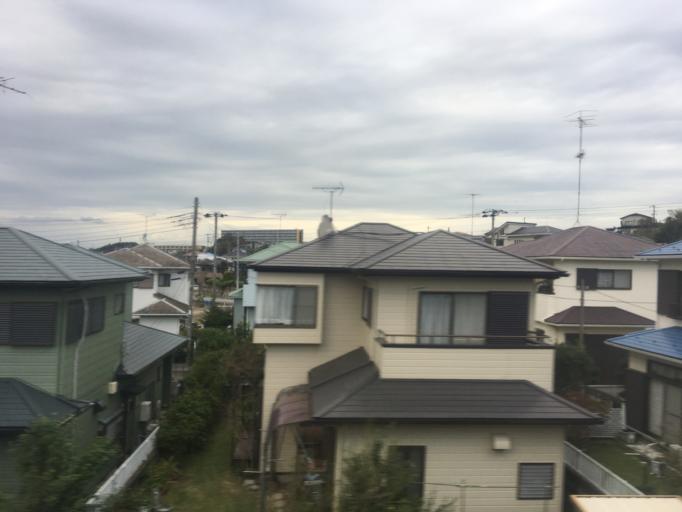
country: JP
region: Chiba
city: Kimitsu
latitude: 35.3435
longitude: 139.9144
